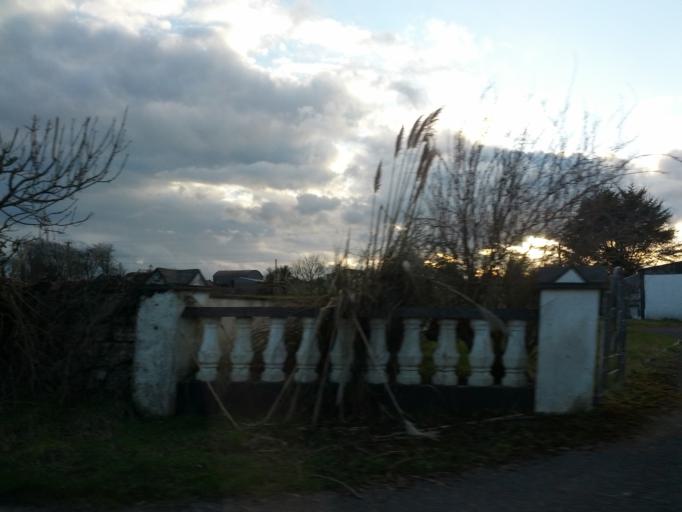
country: IE
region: Connaught
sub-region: County Galway
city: Athenry
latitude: 53.4220
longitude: -8.6890
